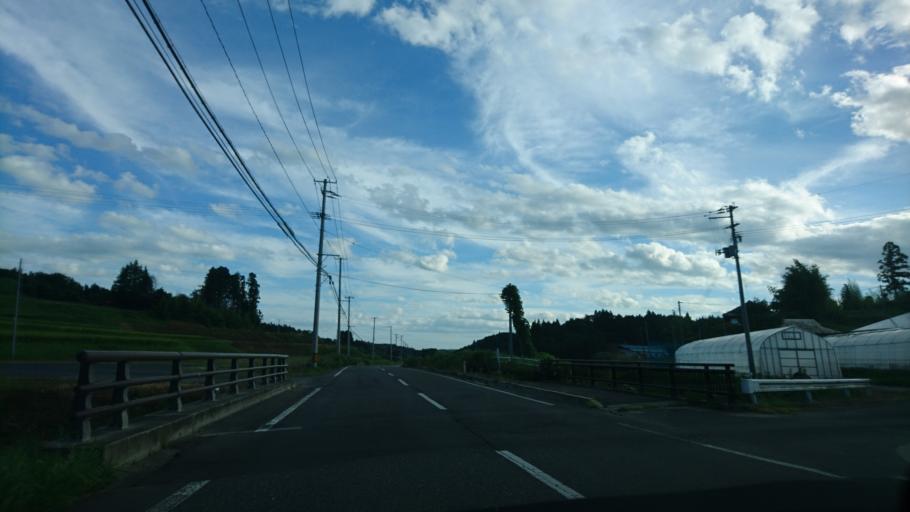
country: JP
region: Iwate
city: Ichinoseki
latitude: 38.8626
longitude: 141.1857
